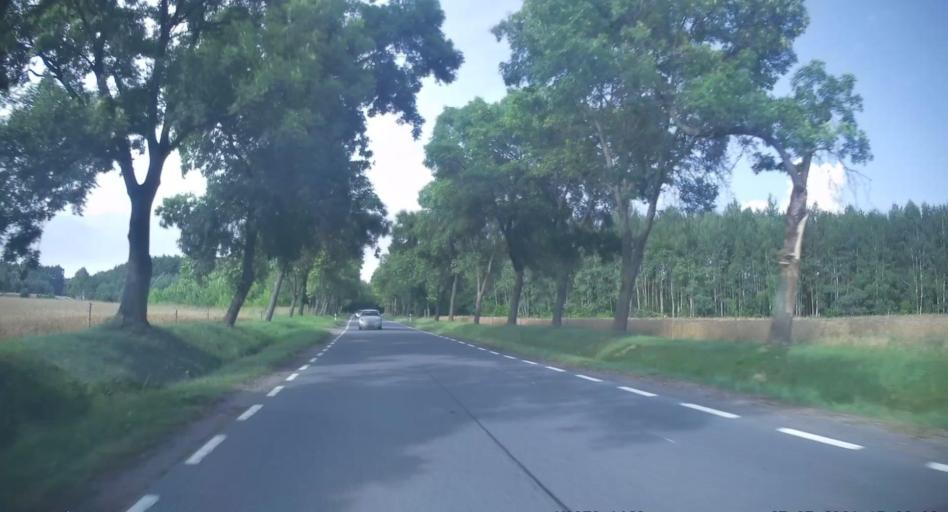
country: PL
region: Lodz Voivodeship
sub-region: Powiat tomaszowski
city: Inowlodz
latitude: 51.5355
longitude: 20.2313
